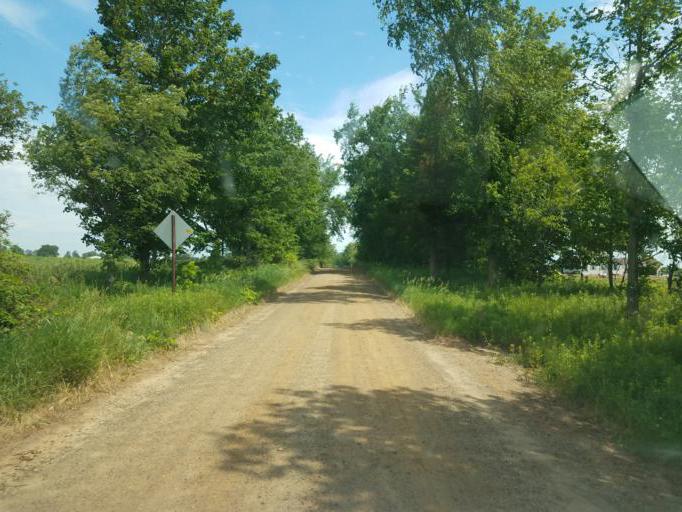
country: US
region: Michigan
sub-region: Barry County
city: Nashville
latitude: 42.6570
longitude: -84.9560
